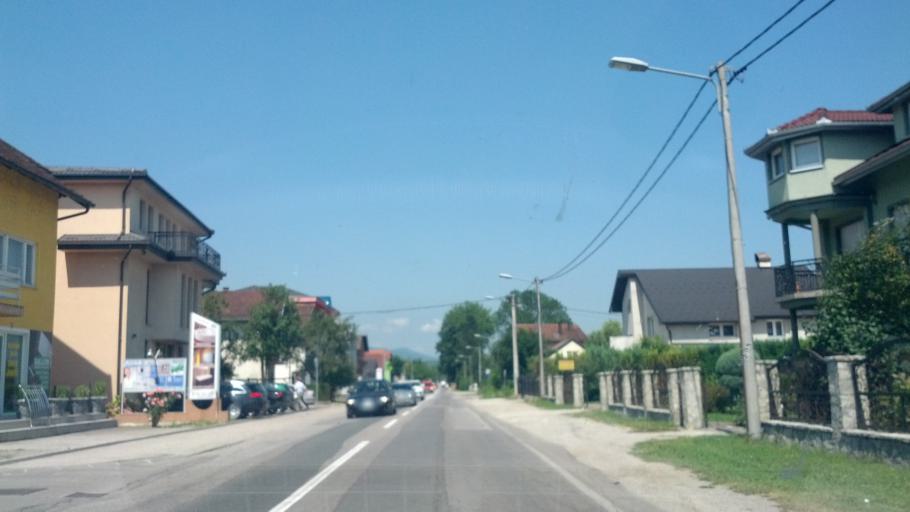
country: BA
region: Federation of Bosnia and Herzegovina
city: Bihac
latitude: 44.8234
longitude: 15.8515
